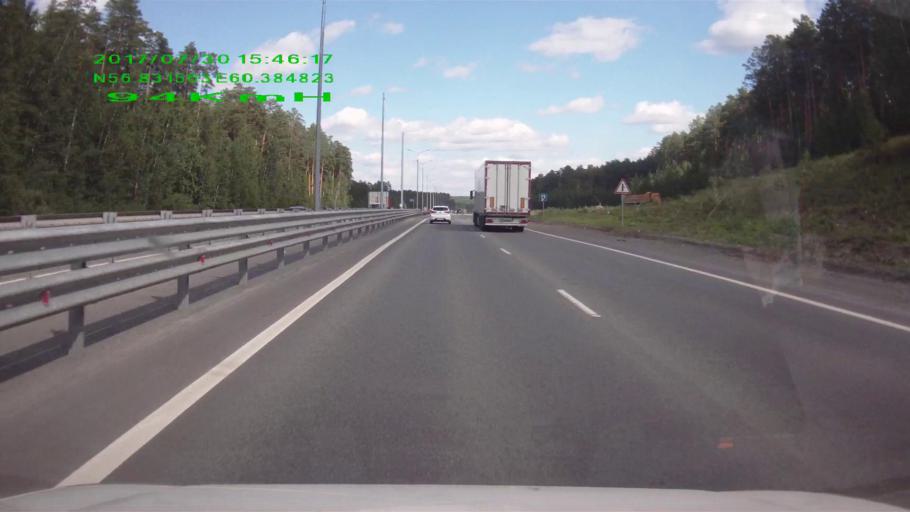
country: RU
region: Sverdlovsk
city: Severka
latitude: 56.8315
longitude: 60.3858
